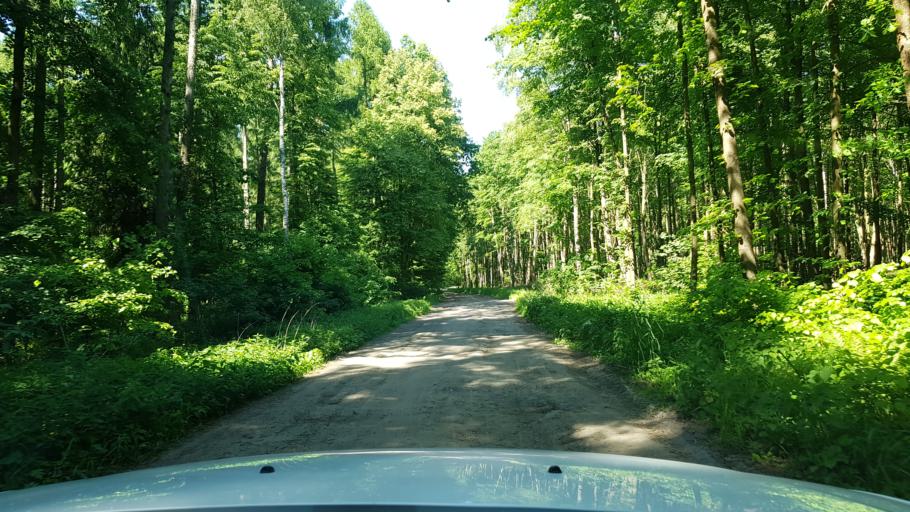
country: PL
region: West Pomeranian Voivodeship
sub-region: Powiat gryfinski
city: Banie
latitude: 53.1187
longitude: 14.5417
